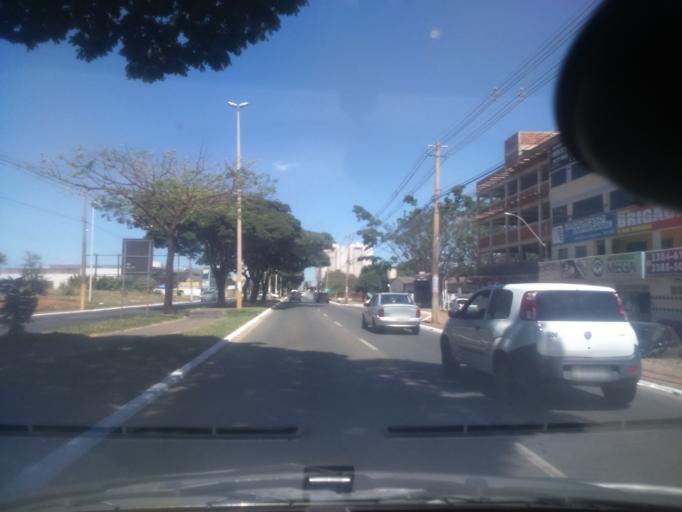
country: BR
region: Federal District
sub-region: Brasilia
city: Brasilia
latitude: -16.0059
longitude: -48.0598
